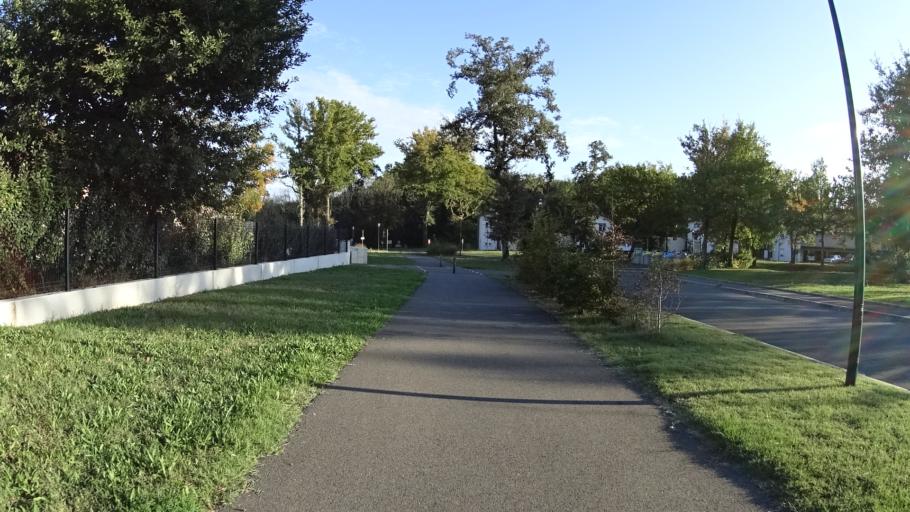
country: FR
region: Aquitaine
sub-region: Departement des Landes
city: Saint-Paul-les-Dax
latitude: 43.7389
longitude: -1.0457
